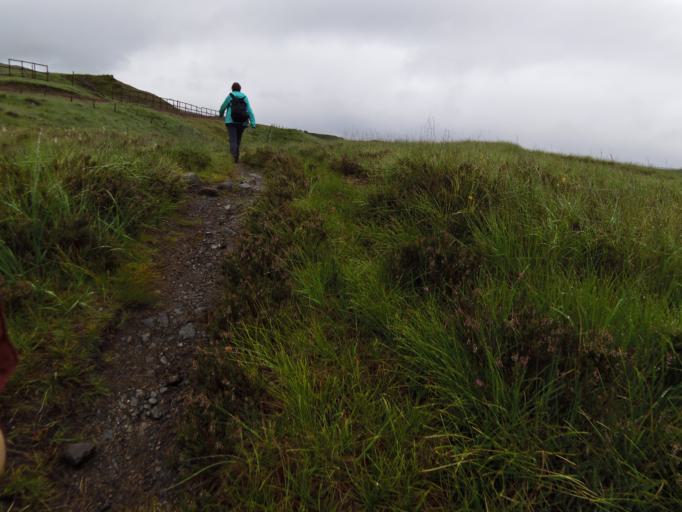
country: GB
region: Scotland
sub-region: Highland
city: Spean Bridge
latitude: 56.7711
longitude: -4.7092
